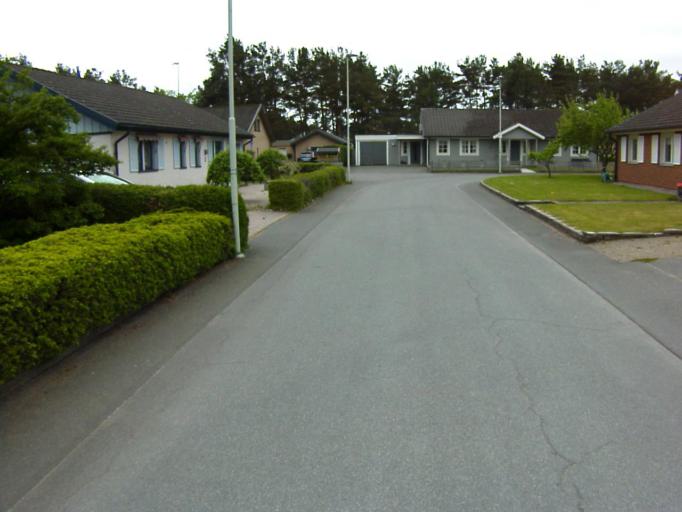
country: SE
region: Skane
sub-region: Kristianstads Kommun
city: Ahus
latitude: 55.9398
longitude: 14.2716
